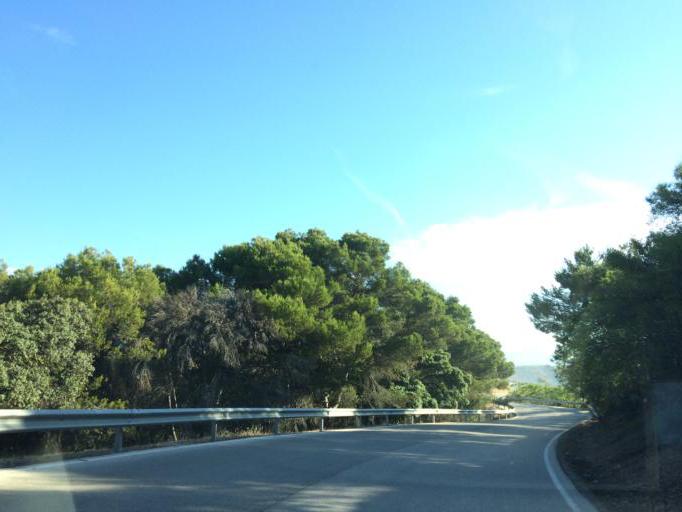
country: ES
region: Andalusia
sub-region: Provincia de Malaga
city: Colmenar
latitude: 36.8666
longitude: -4.3478
